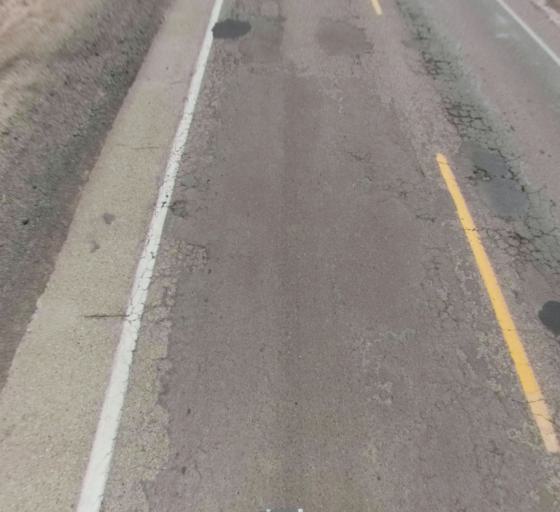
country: US
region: California
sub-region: Fresno County
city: Mendota
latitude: 36.8510
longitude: -120.2701
